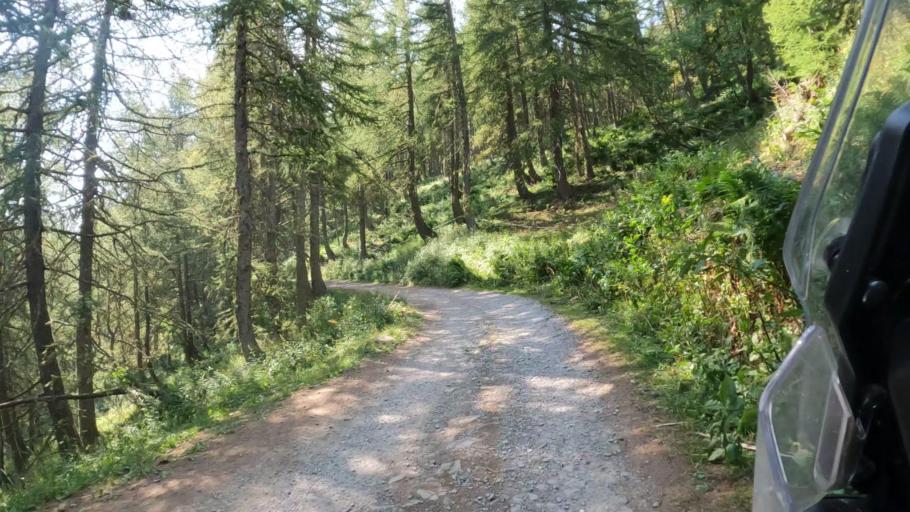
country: IT
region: Piedmont
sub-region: Provincia di Cuneo
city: Briga Alta
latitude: 44.0858
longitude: 7.7297
